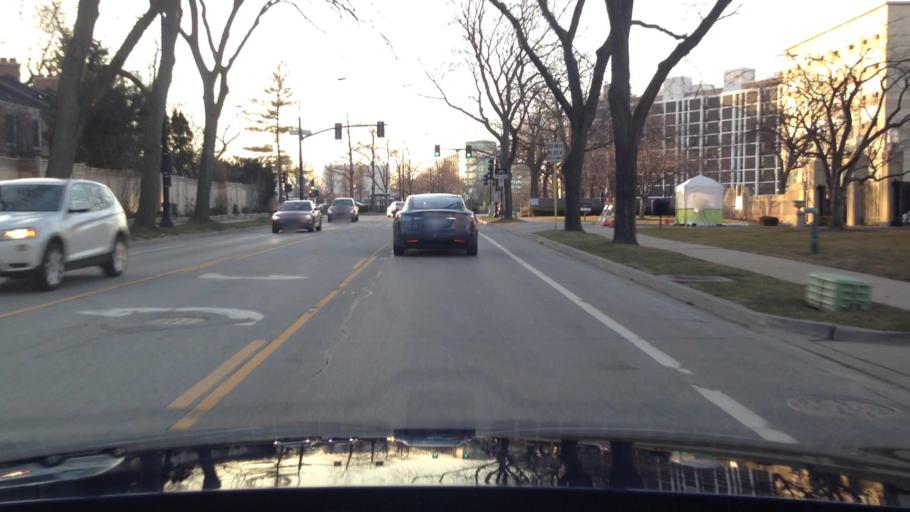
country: US
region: Illinois
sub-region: Cook County
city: Kenilworth
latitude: 42.0857
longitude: -87.6988
